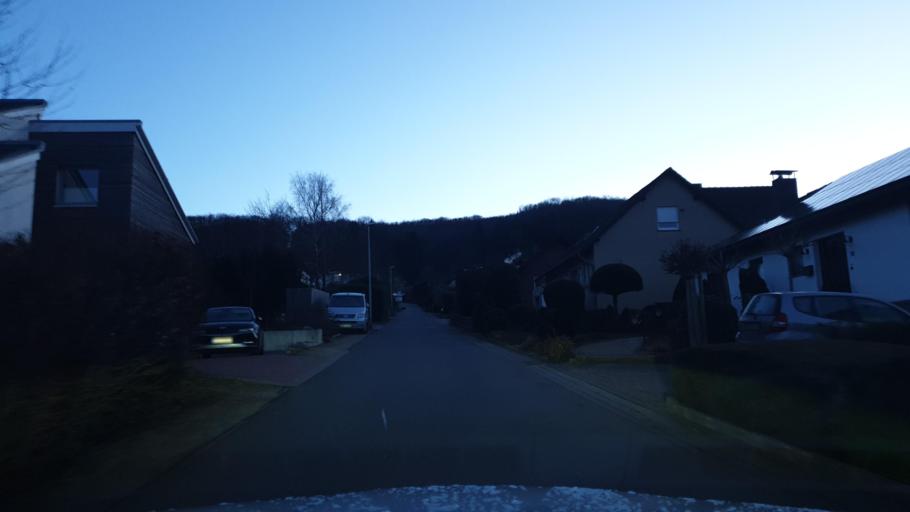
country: DE
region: North Rhine-Westphalia
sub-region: Regierungsbezirk Detmold
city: Minden
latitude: 52.2593
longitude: 8.8638
